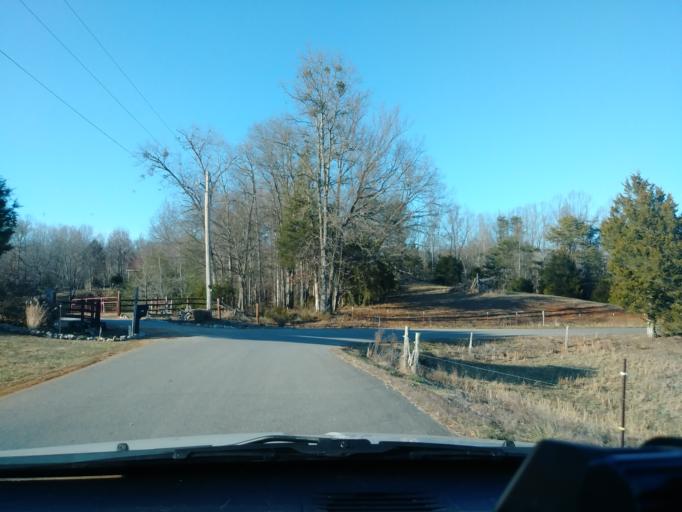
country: US
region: Tennessee
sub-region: Greene County
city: Greeneville
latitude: 36.0825
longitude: -82.9095
